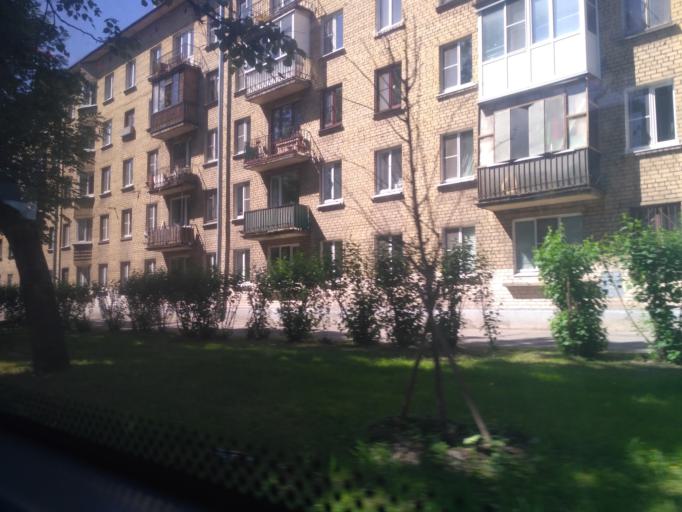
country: RU
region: Leningrad
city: Kalininskiy
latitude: 59.9610
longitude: 30.4224
